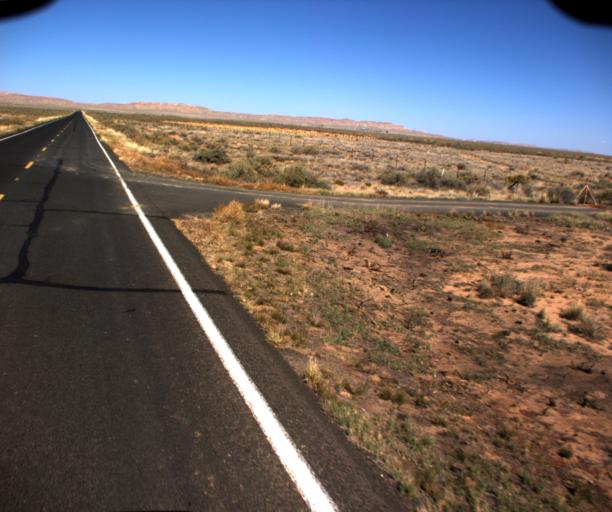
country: US
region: Arizona
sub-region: Navajo County
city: First Mesa
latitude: 35.7115
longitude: -110.5116
